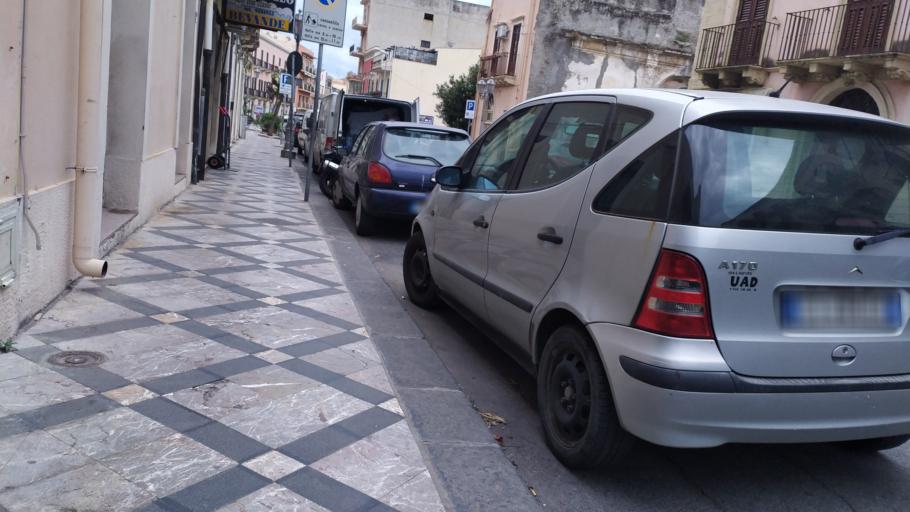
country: IT
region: Sicily
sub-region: Messina
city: Milazzo
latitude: 38.2220
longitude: 15.2408
